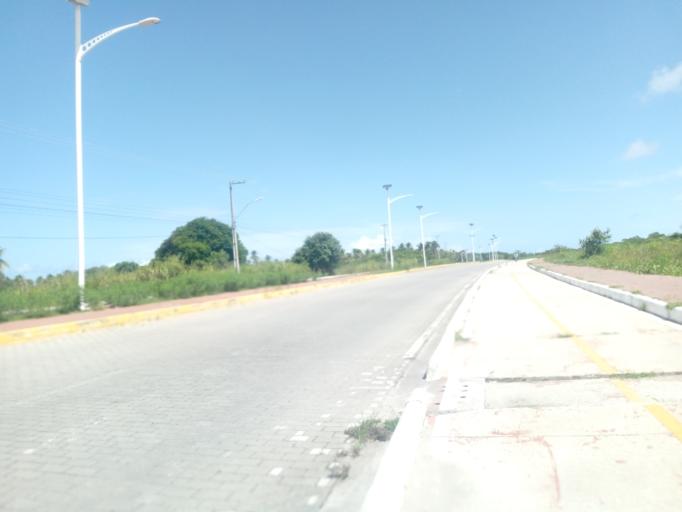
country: BR
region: Pernambuco
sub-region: Ipojuca
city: Ipojuca
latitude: -8.5151
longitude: -35.0098
